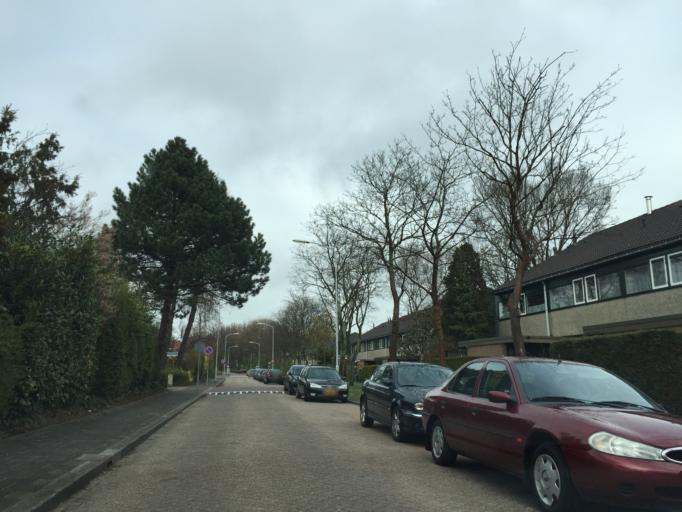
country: NL
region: South Holland
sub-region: Gemeente Leidschendam-Voorburg
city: Voorburg
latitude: 52.0769
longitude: 4.3983
